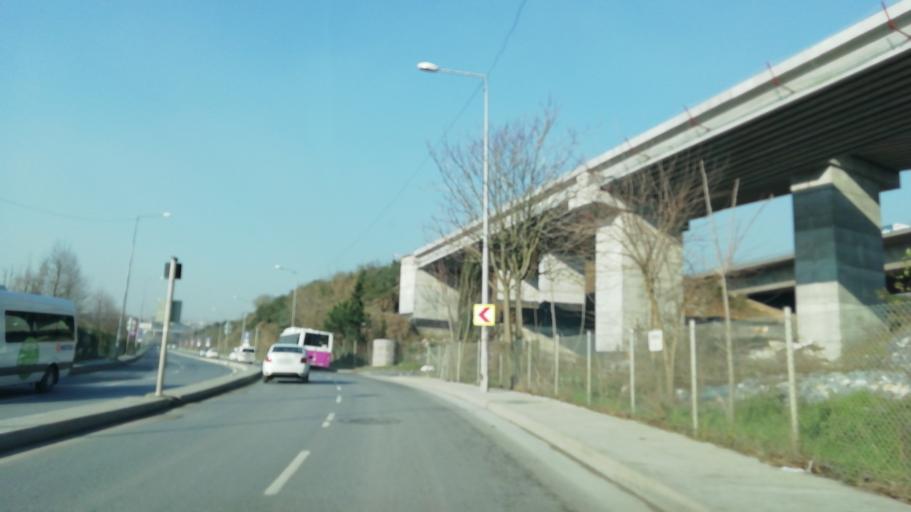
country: TR
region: Istanbul
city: Sisli
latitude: 41.0921
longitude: 28.9336
